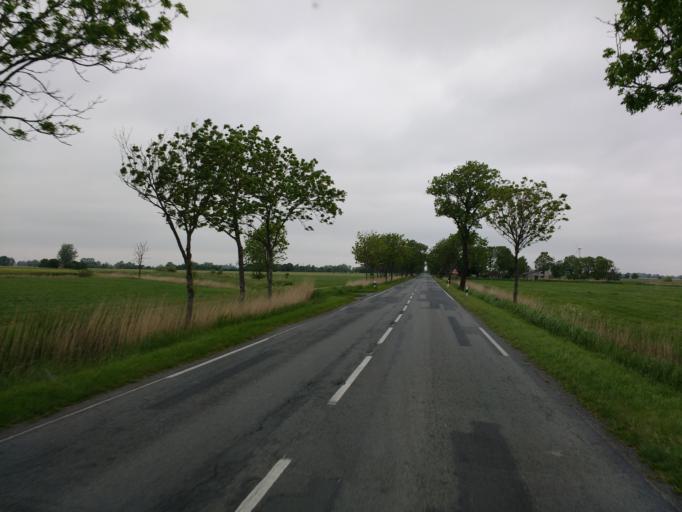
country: DE
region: Lower Saxony
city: Jever
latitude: 53.6392
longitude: 7.9256
